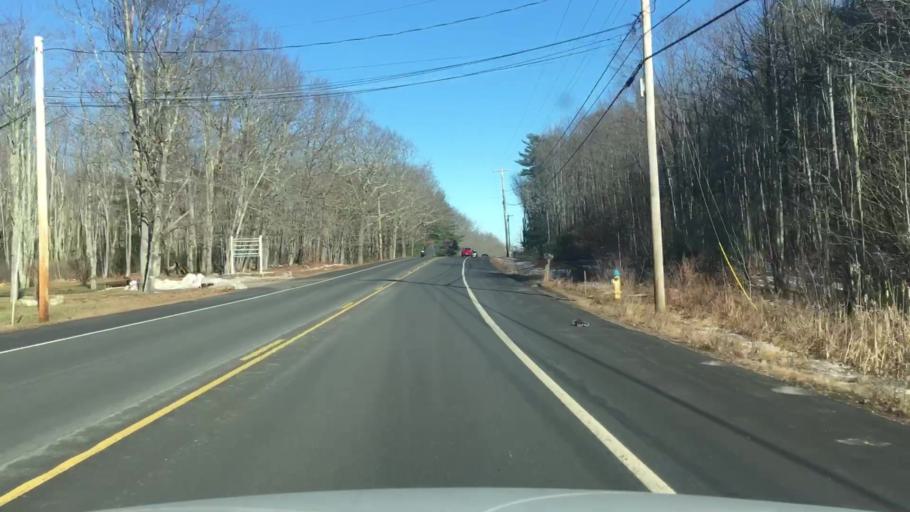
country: US
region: Maine
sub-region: York County
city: Arundel
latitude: 43.4440
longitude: -70.5014
